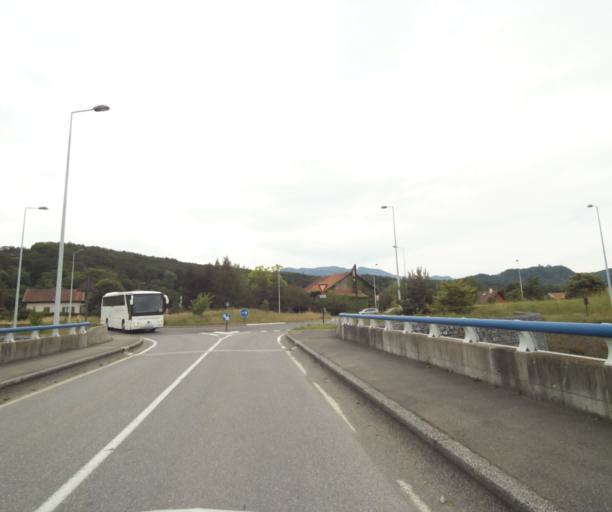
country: FR
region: Rhone-Alpes
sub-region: Departement de la Haute-Savoie
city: Thonon-les-Bains
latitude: 46.3531
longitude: 6.4771
